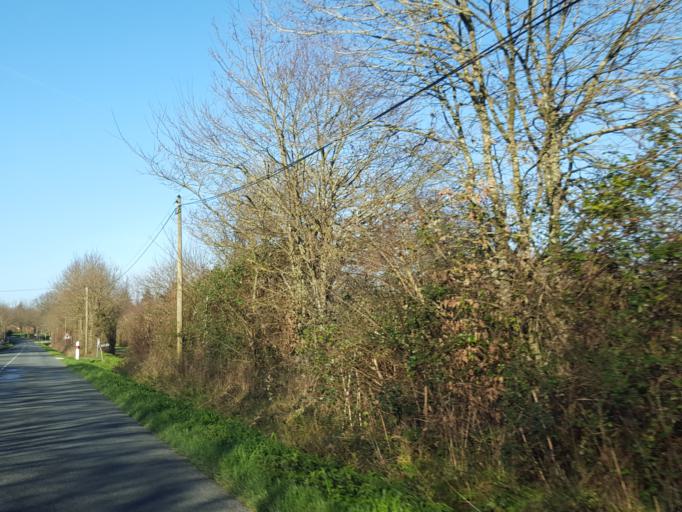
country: FR
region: Pays de la Loire
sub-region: Departement de la Vendee
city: Venansault
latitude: 46.6782
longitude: -1.4900
